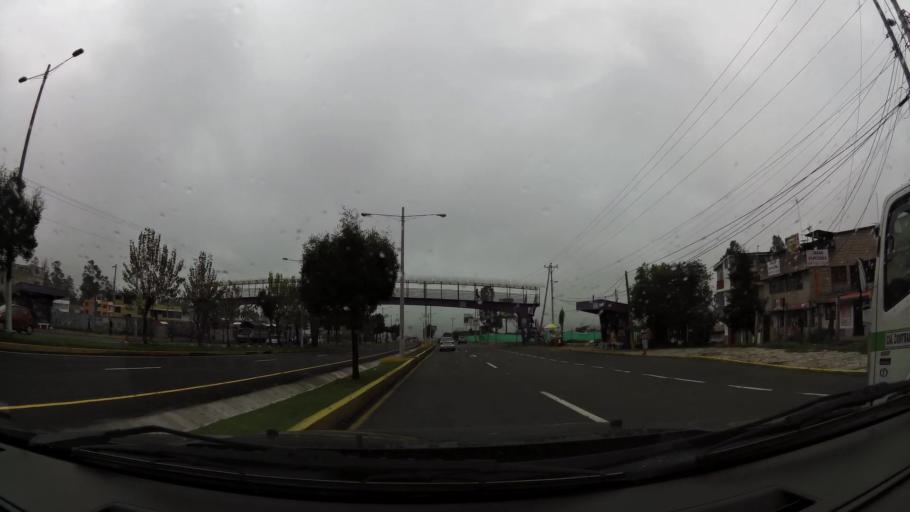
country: EC
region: Pichincha
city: Sangolqui
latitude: -0.2785
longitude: -78.4816
